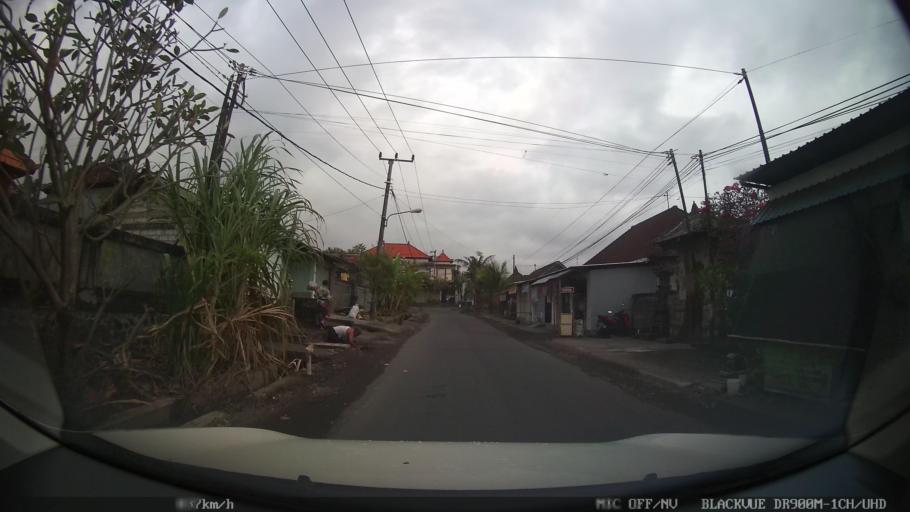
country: ID
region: Bali
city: Banjar Pasekan
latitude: -8.6395
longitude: 115.2754
